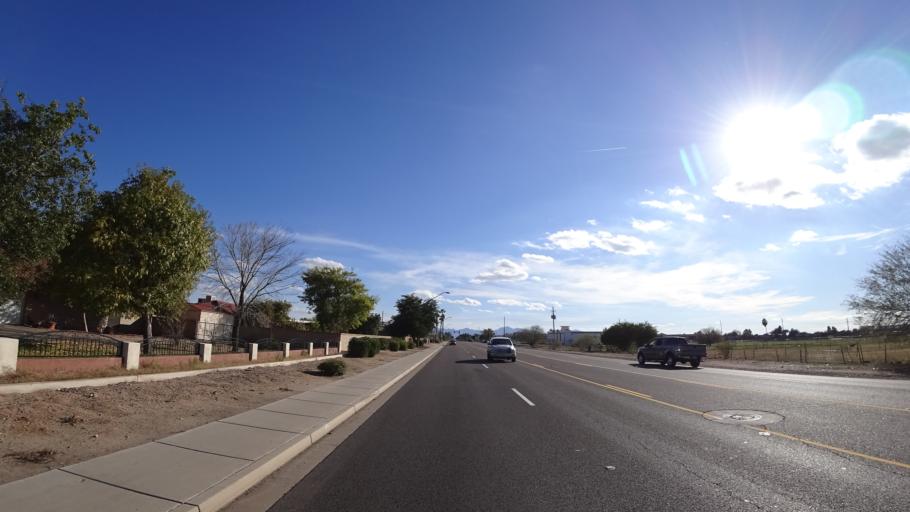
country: US
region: Arizona
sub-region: Maricopa County
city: Glendale
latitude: 33.5112
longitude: -112.2376
